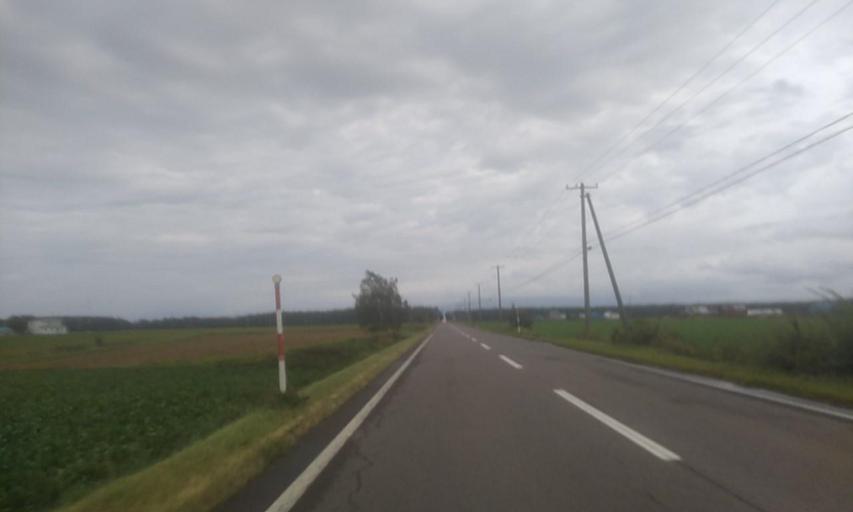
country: JP
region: Hokkaido
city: Abashiri
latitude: 43.8936
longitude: 144.5166
